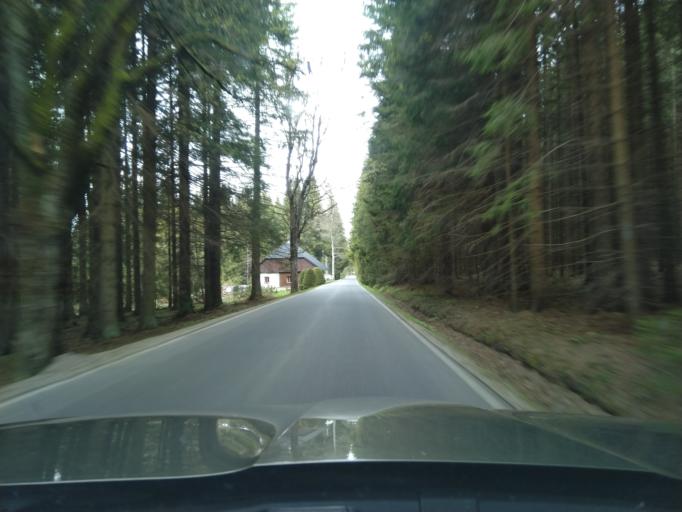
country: CZ
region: Jihocesky
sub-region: Okres Prachatice
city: Borova Lada
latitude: 49.0183
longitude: 13.6666
